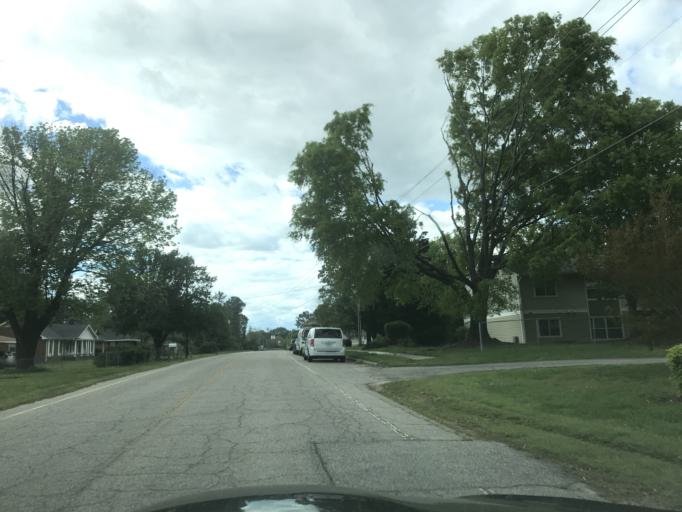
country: US
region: North Carolina
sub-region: Wake County
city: Raleigh
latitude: 35.8386
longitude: -78.5732
